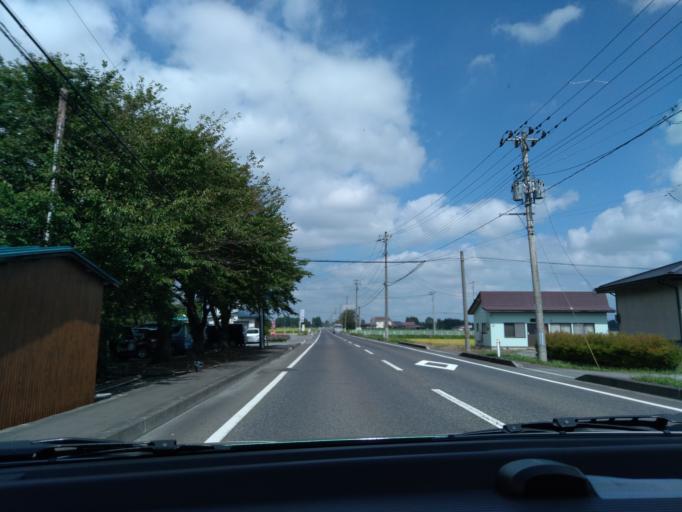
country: JP
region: Iwate
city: Hanamaki
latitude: 39.3901
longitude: 141.0576
